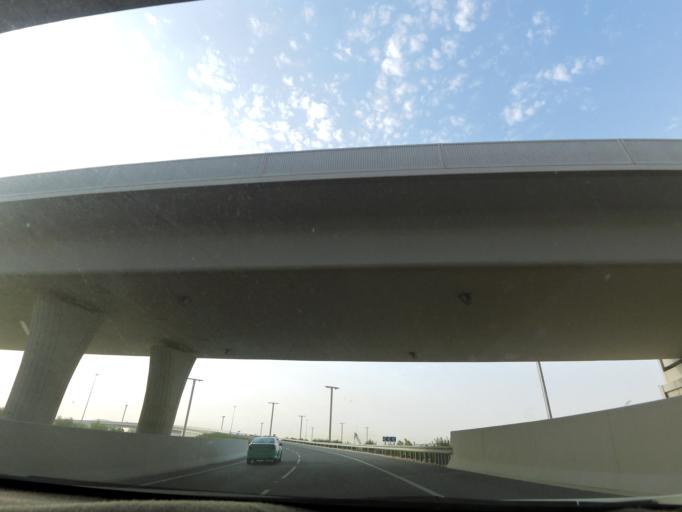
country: QA
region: Al Wakrah
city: Al Wakrah
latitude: 25.2388
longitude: 51.5896
